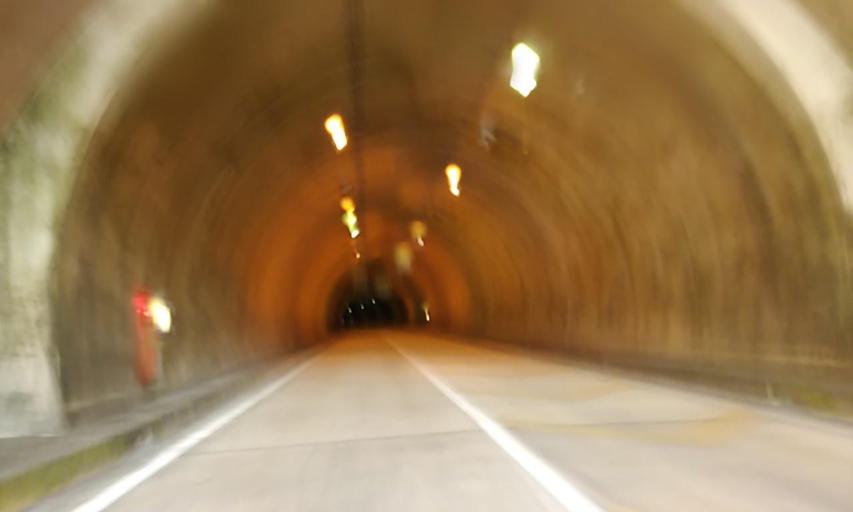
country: JP
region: Wakayama
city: Shingu
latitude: 33.8956
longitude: 135.8796
